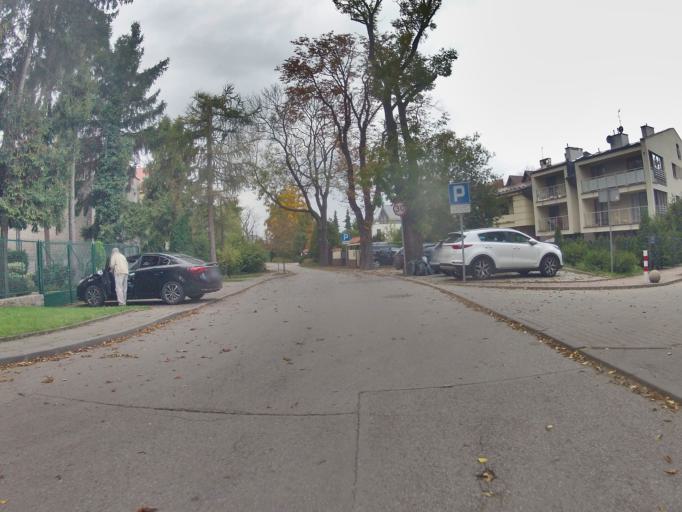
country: PL
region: Lesser Poland Voivodeship
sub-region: Krakow
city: Krakow
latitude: 50.0619
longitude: 19.8914
